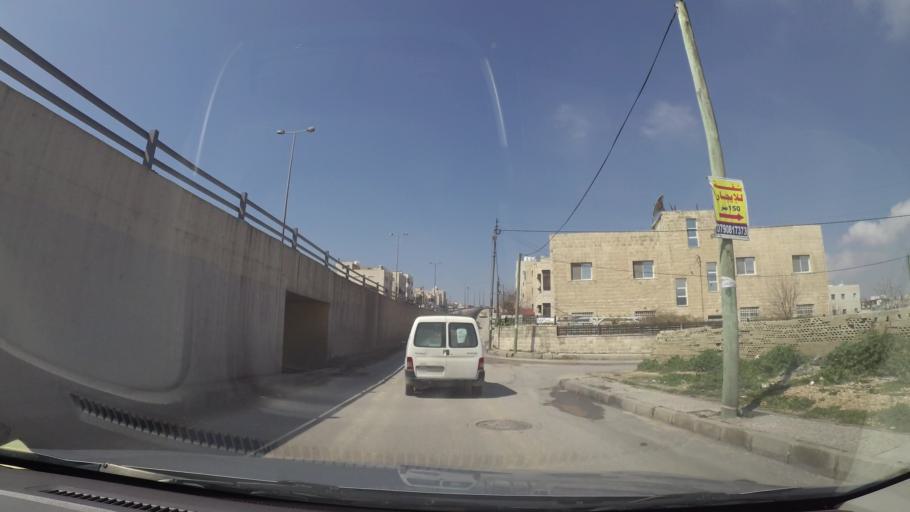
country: JO
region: Amman
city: Al Bunayyat ash Shamaliyah
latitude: 31.9188
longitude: 35.8976
